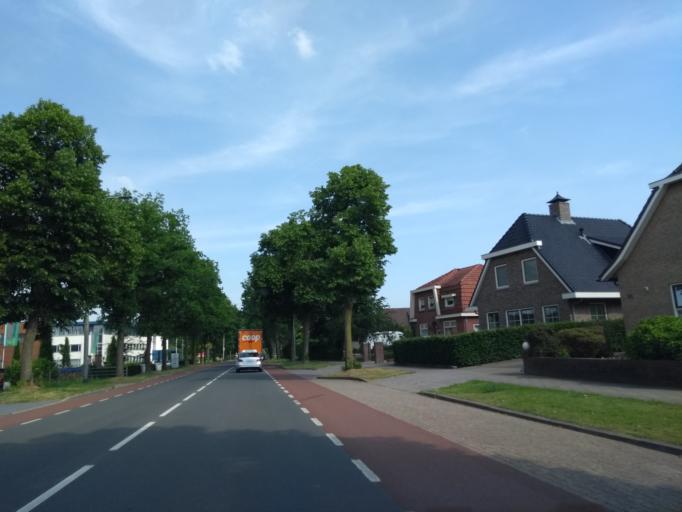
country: DE
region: Lower Saxony
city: Getelo
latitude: 52.4102
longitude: 6.9076
